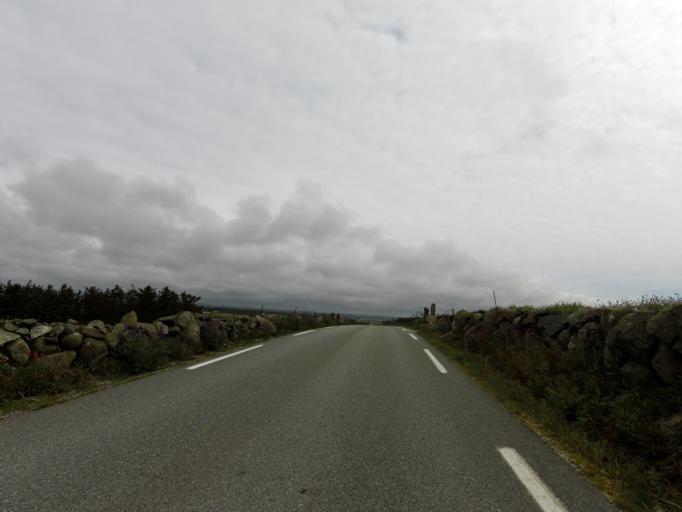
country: NO
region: Rogaland
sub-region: Ha
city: Naerbo
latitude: 58.6580
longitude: 5.5657
